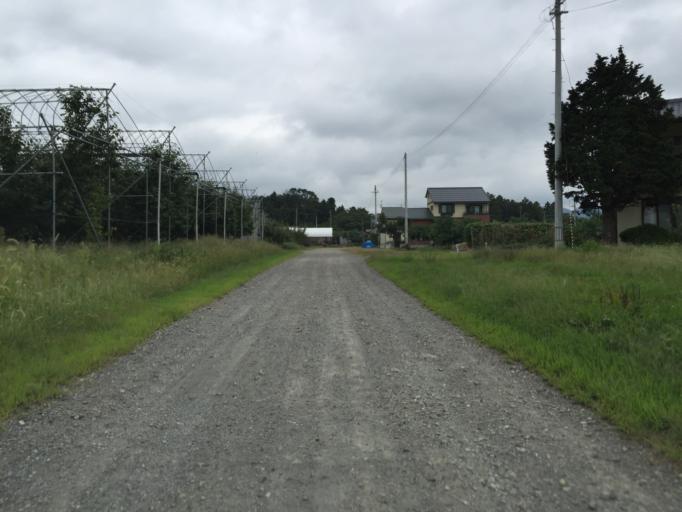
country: JP
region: Fukushima
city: Fukushima-shi
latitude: 37.8118
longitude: 140.4296
